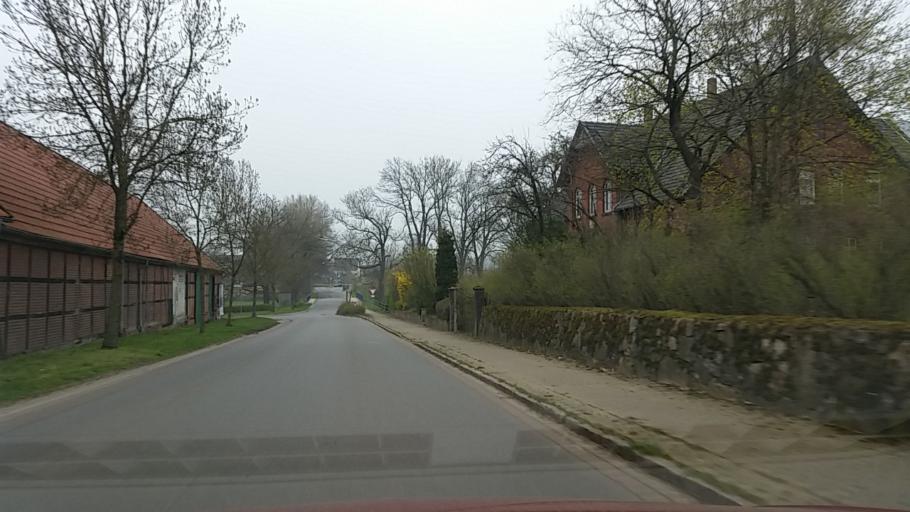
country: DE
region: Lower Saxony
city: Suderburg
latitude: 52.9518
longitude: 10.4832
